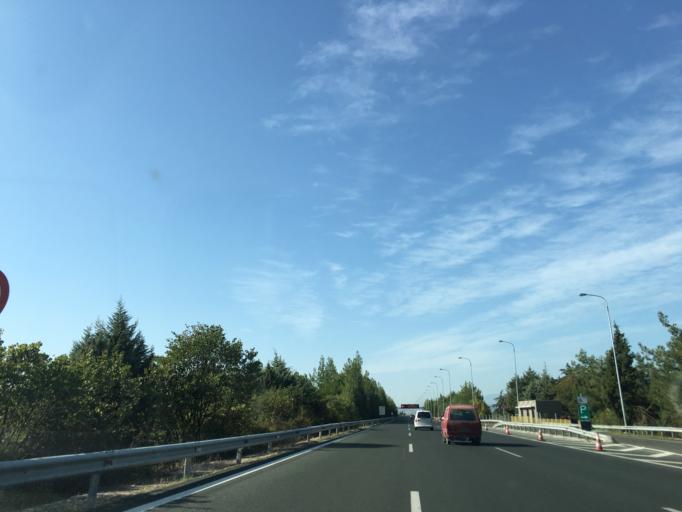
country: GR
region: Central Macedonia
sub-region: Nomos Imathias
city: Kleidi
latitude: 40.5481
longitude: 22.5916
